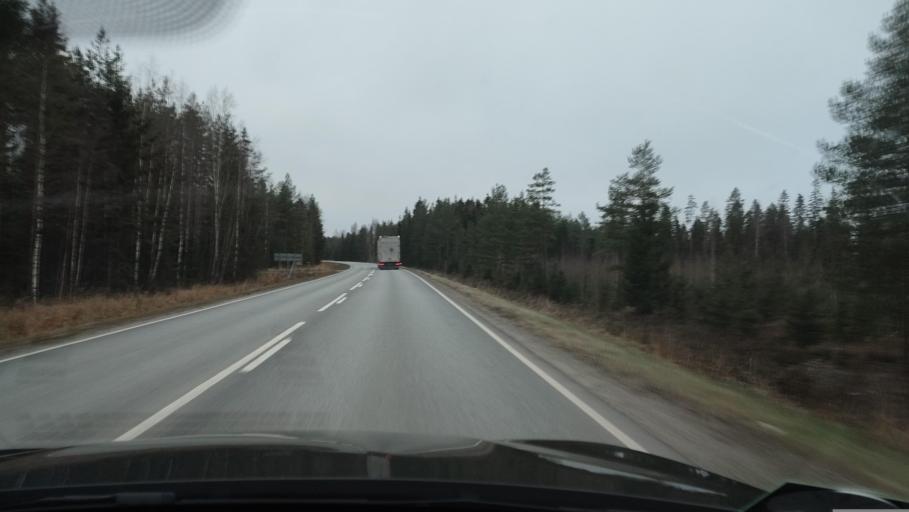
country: FI
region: Southern Ostrobothnia
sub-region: Suupohja
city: Kauhajoki
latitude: 62.3927
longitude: 22.1512
